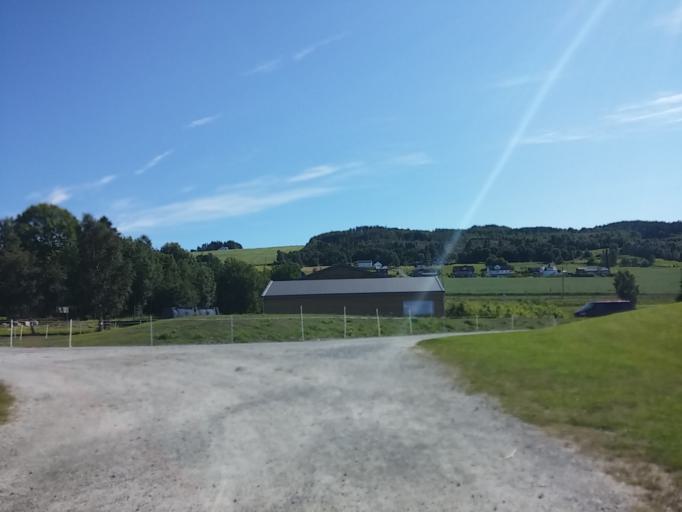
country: NO
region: Sor-Trondelag
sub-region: Malvik
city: Malvik
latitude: 63.4328
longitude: 10.7279
